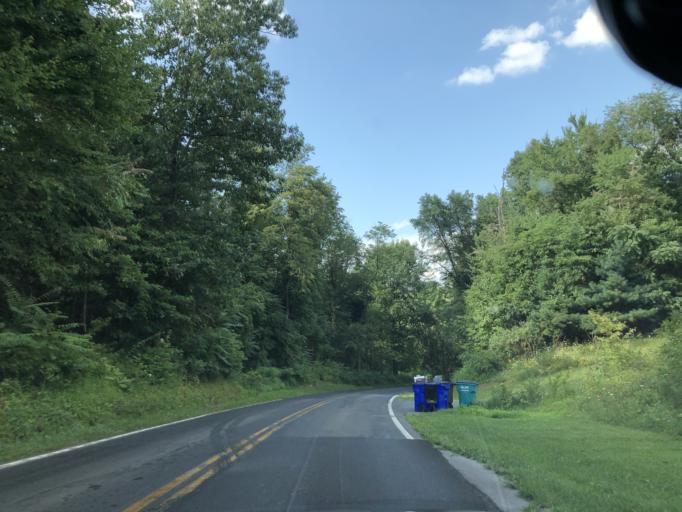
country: US
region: Maryland
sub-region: Carroll County
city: Mount Airy
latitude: 39.4053
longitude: -77.1797
